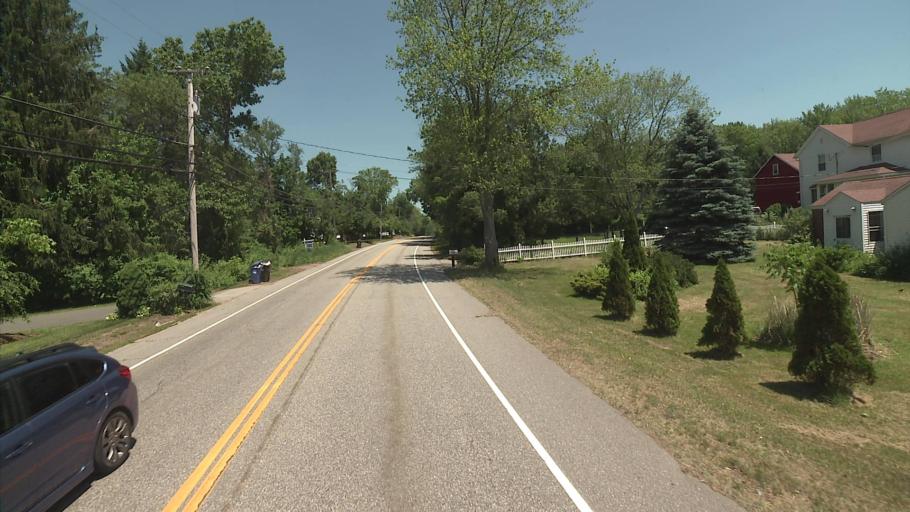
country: US
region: Connecticut
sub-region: Tolland County
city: Tolland
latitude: 41.8801
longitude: -72.4047
